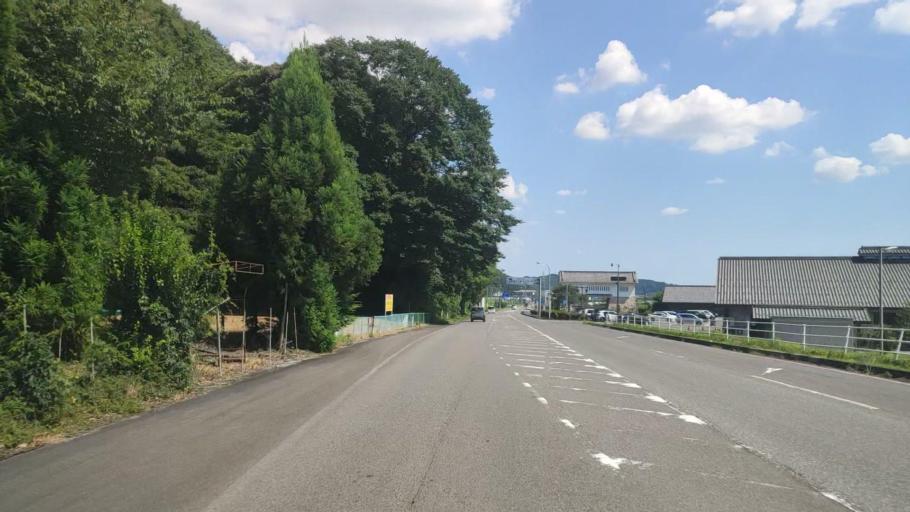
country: JP
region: Gifu
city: Godo
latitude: 35.5009
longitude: 136.6674
